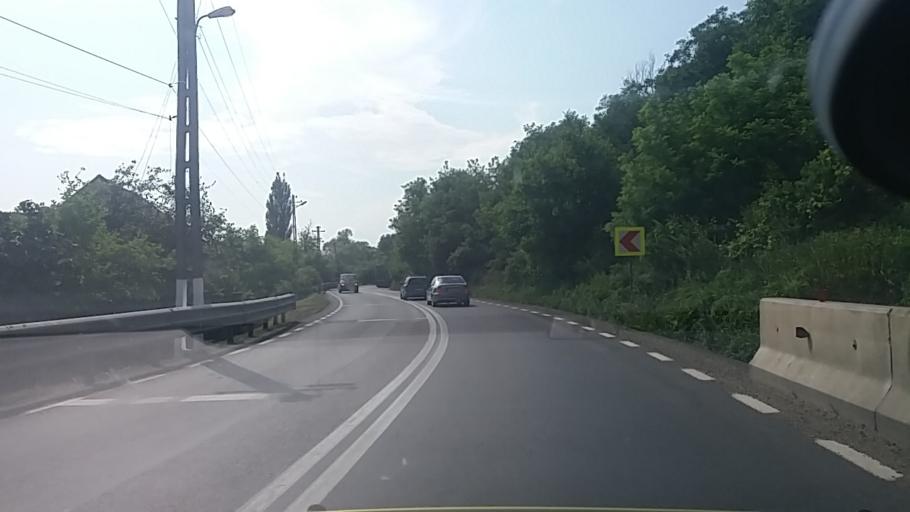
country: RO
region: Arad
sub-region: Comuna Bata
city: Bata
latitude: 46.0335
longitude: 22.0907
